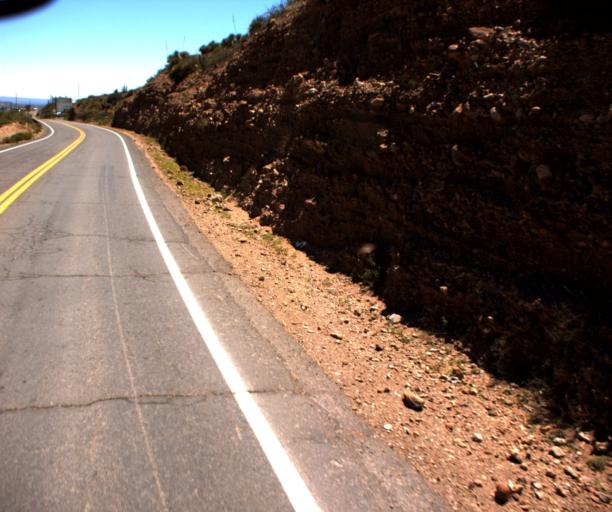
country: US
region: Arizona
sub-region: Greenlee County
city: Morenci
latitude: 33.0624
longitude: -109.3338
